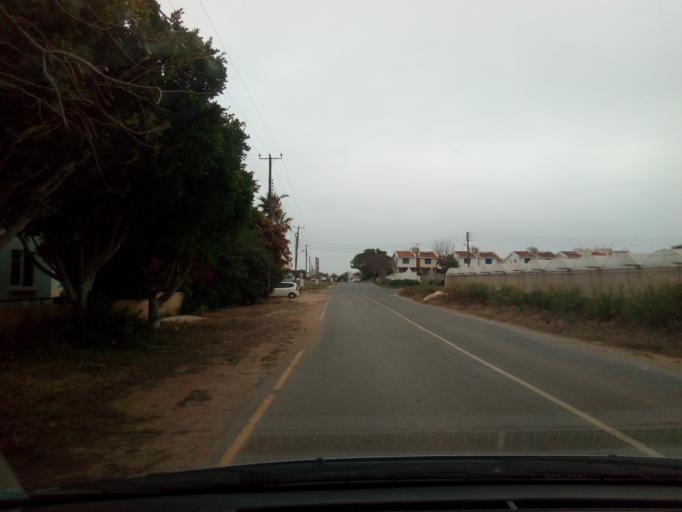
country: CY
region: Ammochostos
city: Paralimni
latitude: 35.0584
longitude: 34.0033
